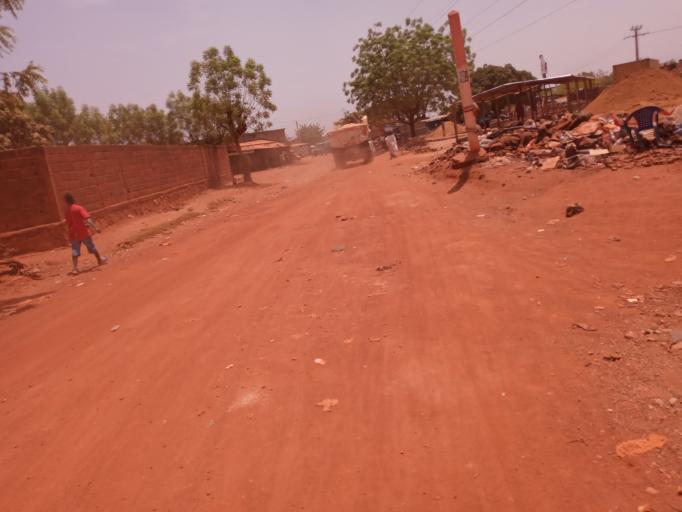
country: ML
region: Bamako
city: Bamako
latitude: 12.5577
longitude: -7.9806
